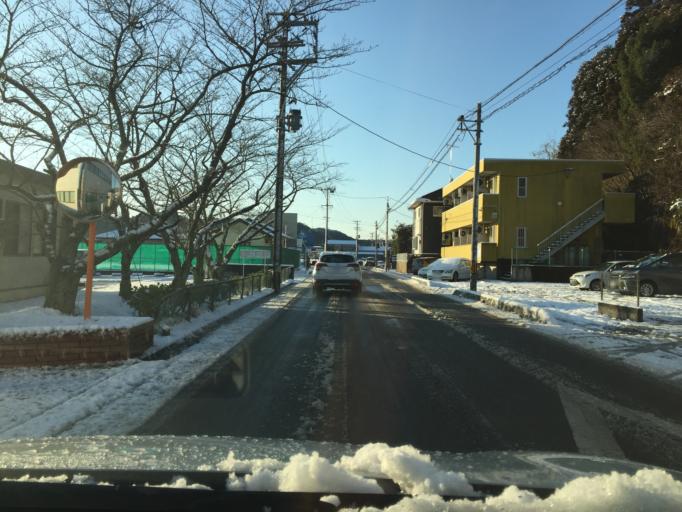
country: JP
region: Fukushima
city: Iwaki
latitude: 37.0604
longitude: 140.9108
